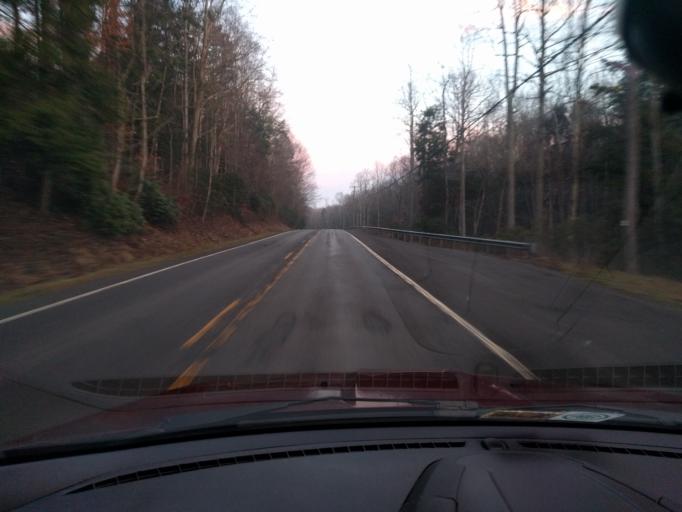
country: US
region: West Virginia
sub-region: Greenbrier County
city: Rainelle
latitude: 38.0332
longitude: -80.9170
